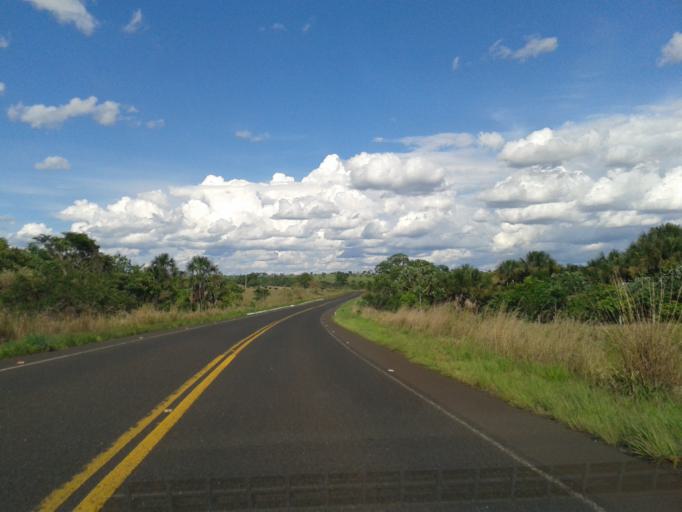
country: BR
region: Minas Gerais
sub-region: Iturama
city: Iturama
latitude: -19.5572
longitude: -49.8702
